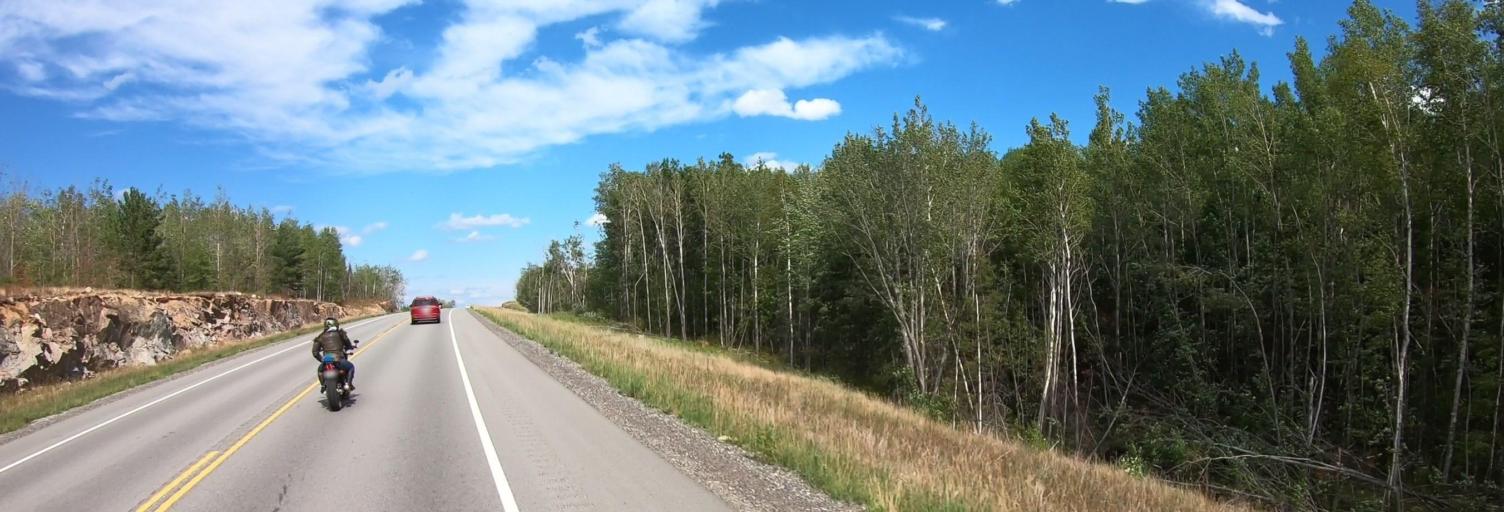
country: US
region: Minnesota
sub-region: Saint Louis County
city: Babbitt
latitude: 47.8420
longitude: -92.1472
